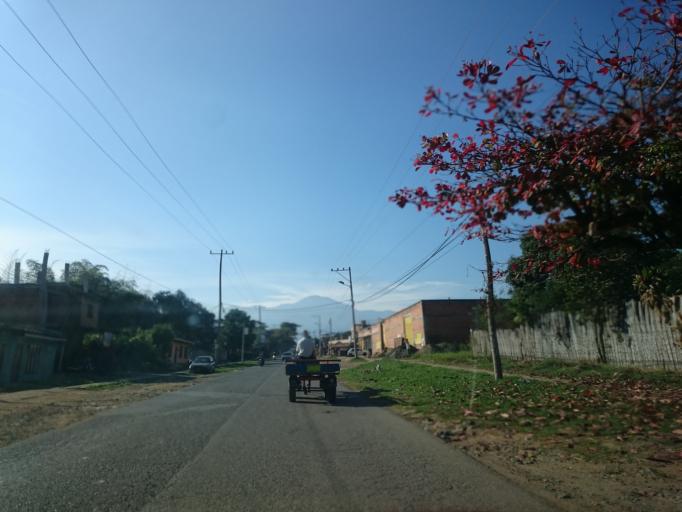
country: CO
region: Cauca
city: Santander de Quilichao
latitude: 3.0160
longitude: -76.4915
